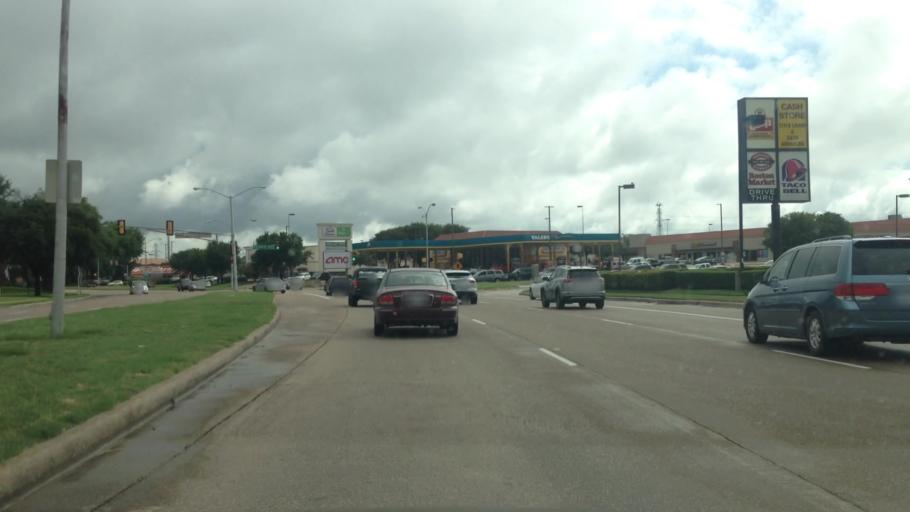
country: US
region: Texas
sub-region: Tarrant County
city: Benbrook
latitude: 32.6639
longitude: -97.4024
